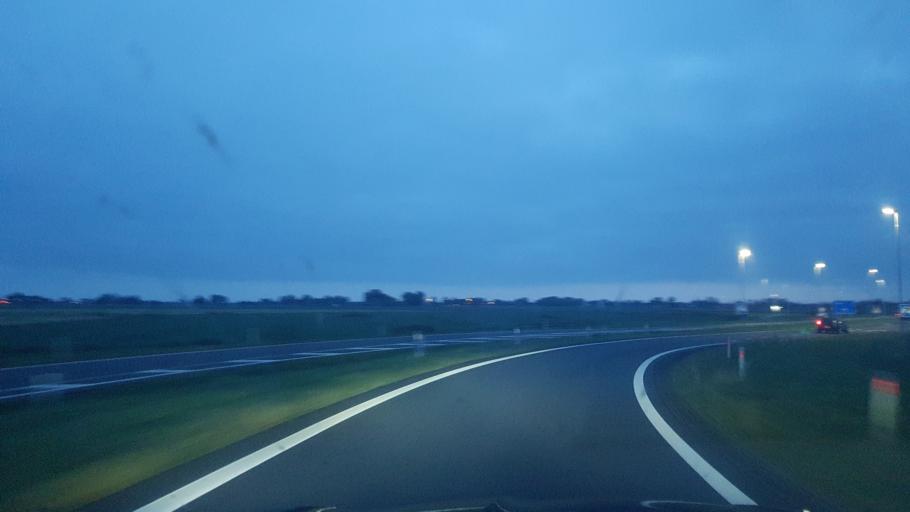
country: NL
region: Friesland
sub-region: Gemeente Boarnsterhim
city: Wergea
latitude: 53.1668
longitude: 5.8337
